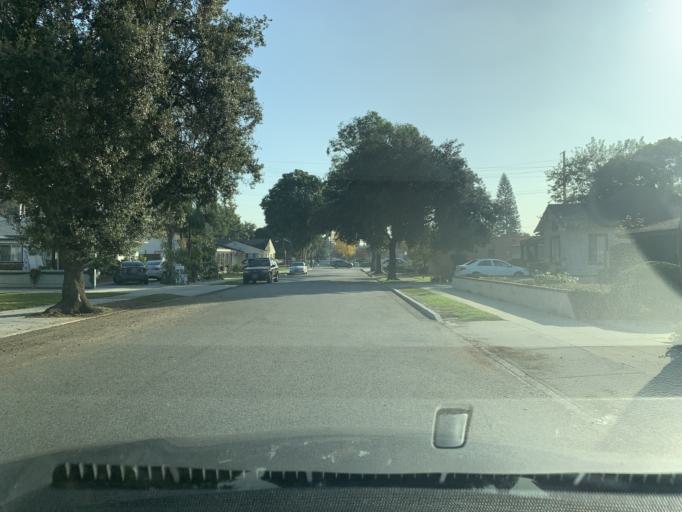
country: US
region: California
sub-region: Los Angeles County
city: Covina
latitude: 34.0908
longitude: -117.8958
